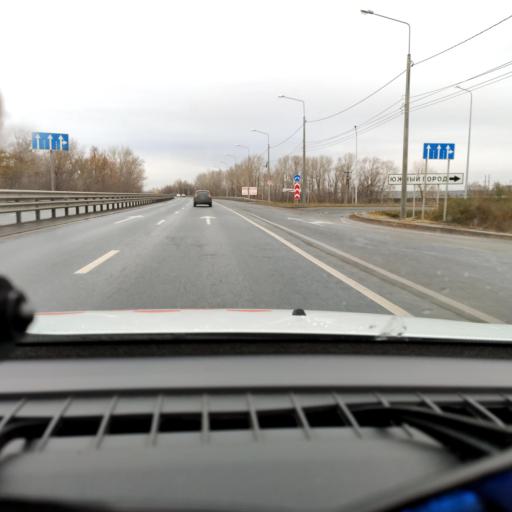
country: RU
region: Samara
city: Samara
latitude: 53.1006
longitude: 50.1609
